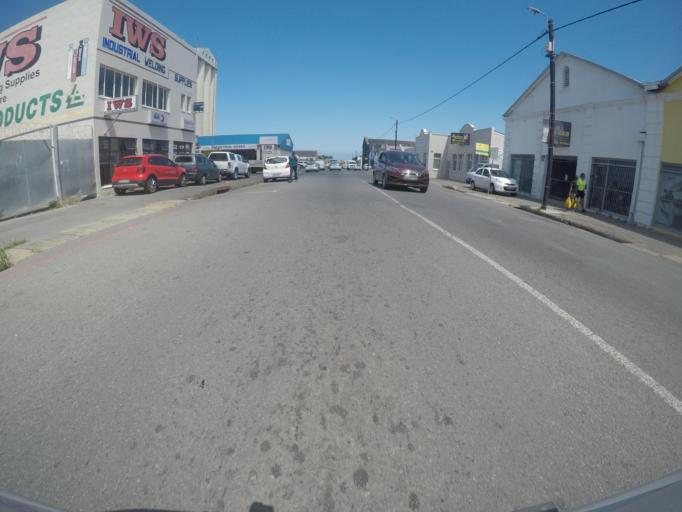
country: ZA
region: Eastern Cape
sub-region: Buffalo City Metropolitan Municipality
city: East London
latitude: -33.0093
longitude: 27.9068
